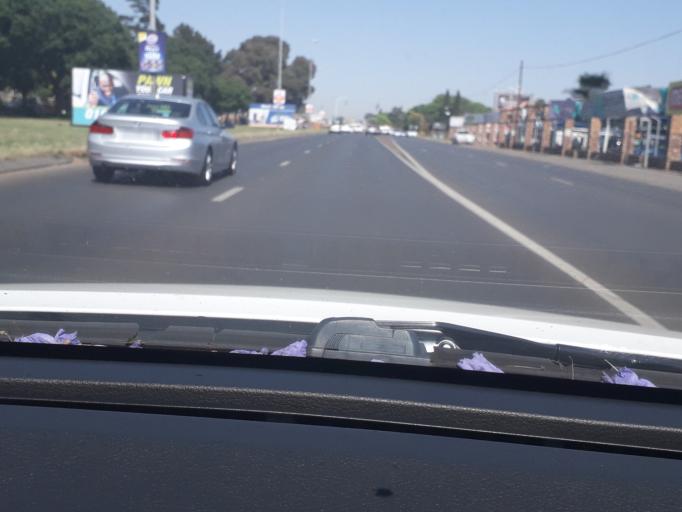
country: ZA
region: Gauteng
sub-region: Ekurhuleni Metropolitan Municipality
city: Boksburg
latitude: -26.1792
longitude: 28.2694
